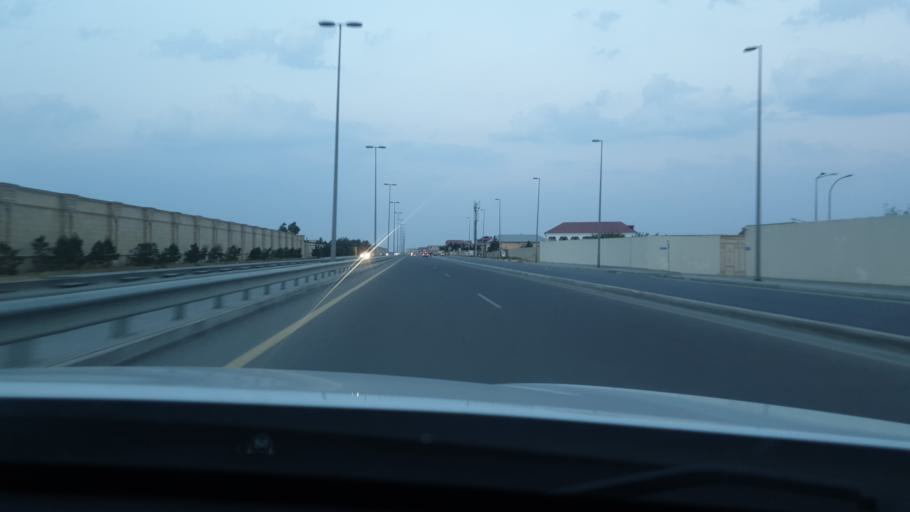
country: AZ
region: Baki
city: Bilajer
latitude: 40.5838
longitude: 50.0193
